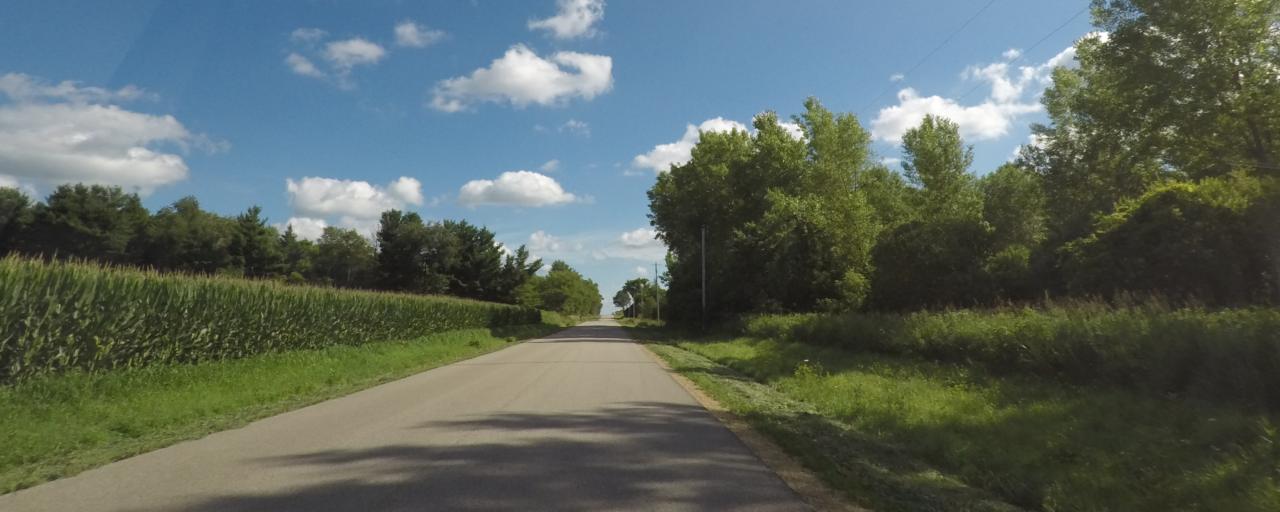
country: US
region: Wisconsin
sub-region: Dane County
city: Stoughton
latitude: 42.9045
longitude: -89.1319
